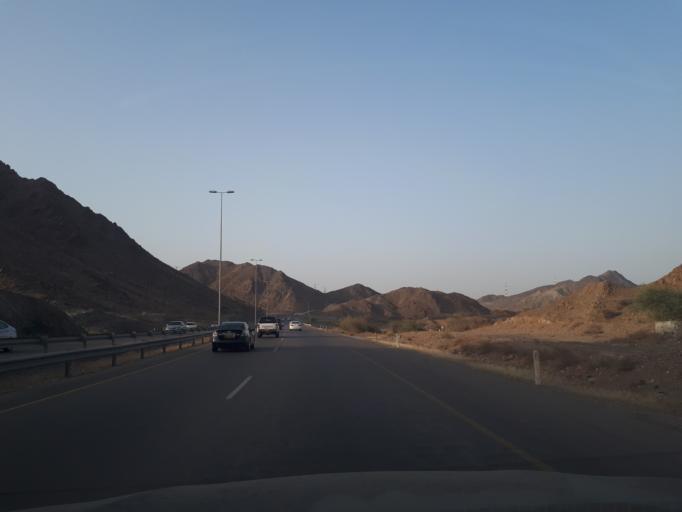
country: OM
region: Muhafazat ad Dakhiliyah
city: Bidbid
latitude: 23.4618
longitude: 58.1868
